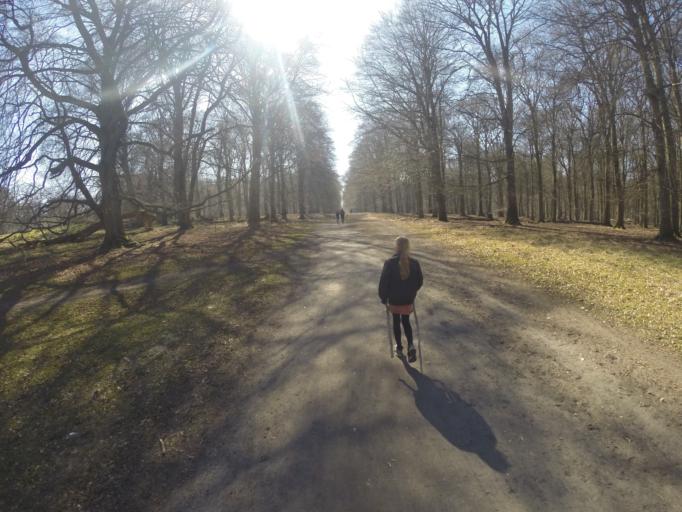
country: DK
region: Capital Region
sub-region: Gentofte Kommune
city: Charlottenlund
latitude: 55.7848
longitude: 12.5573
